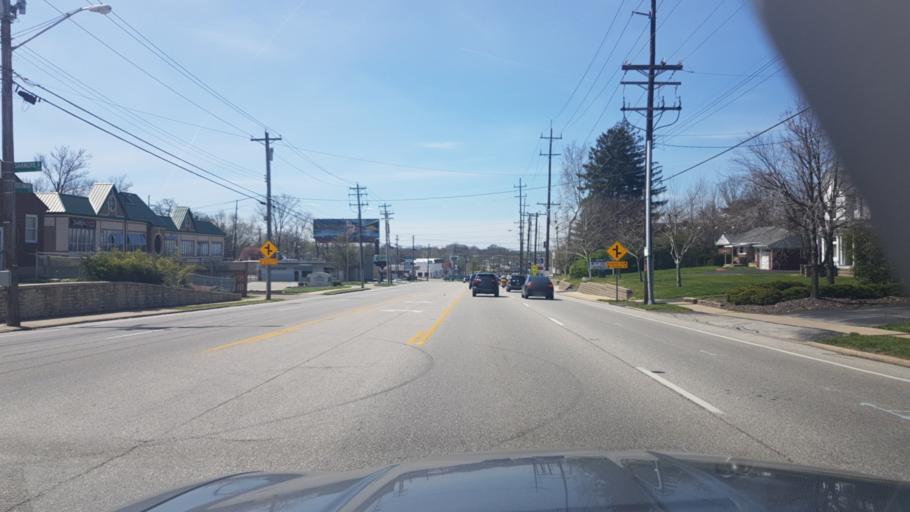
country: US
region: Ohio
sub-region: Hamilton County
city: Fruit Hill
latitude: 39.0729
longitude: -84.3559
